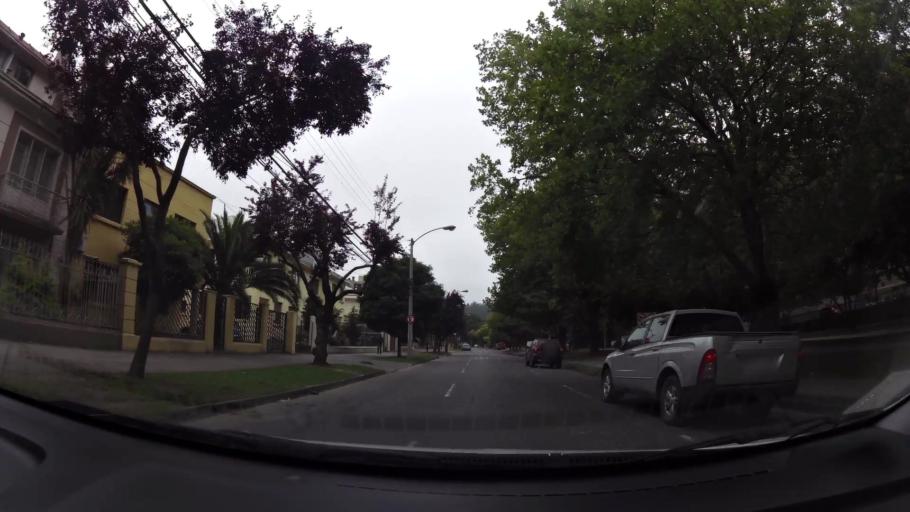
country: CL
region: Biobio
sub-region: Provincia de Concepcion
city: Concepcion
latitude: -36.8305
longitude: -73.0433
